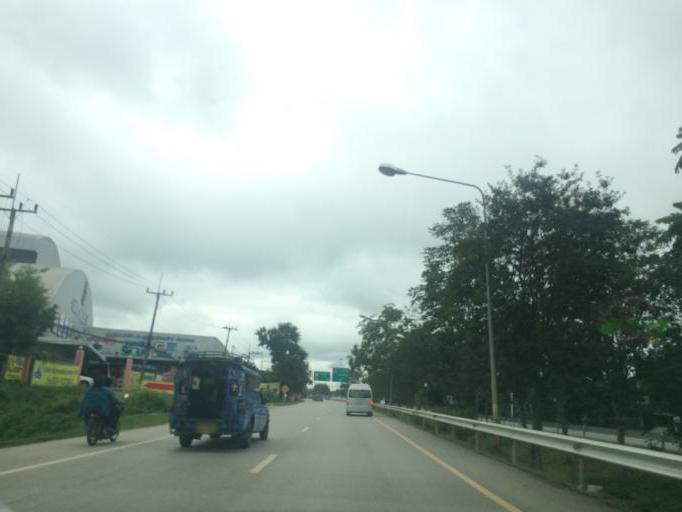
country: TH
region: Chiang Rai
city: Chiang Rai
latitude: 19.8475
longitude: 99.8058
